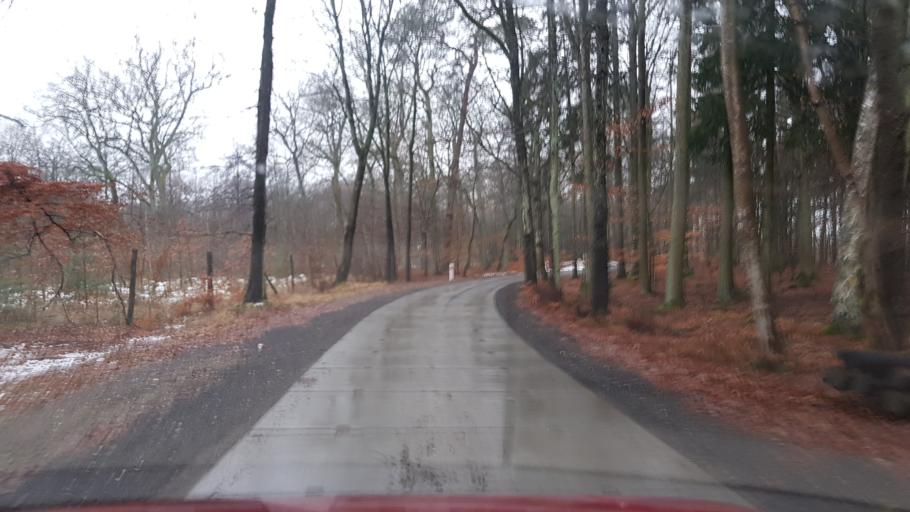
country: PL
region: West Pomeranian Voivodeship
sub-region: Powiat policki
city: Dobra
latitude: 53.5505
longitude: 14.4134
